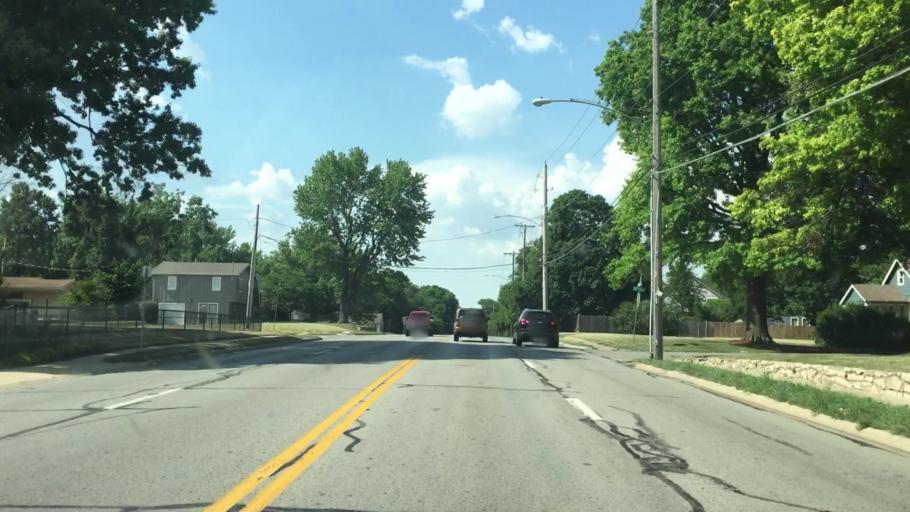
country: US
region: Kansas
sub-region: Johnson County
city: Merriam
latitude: 39.0009
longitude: -94.7145
